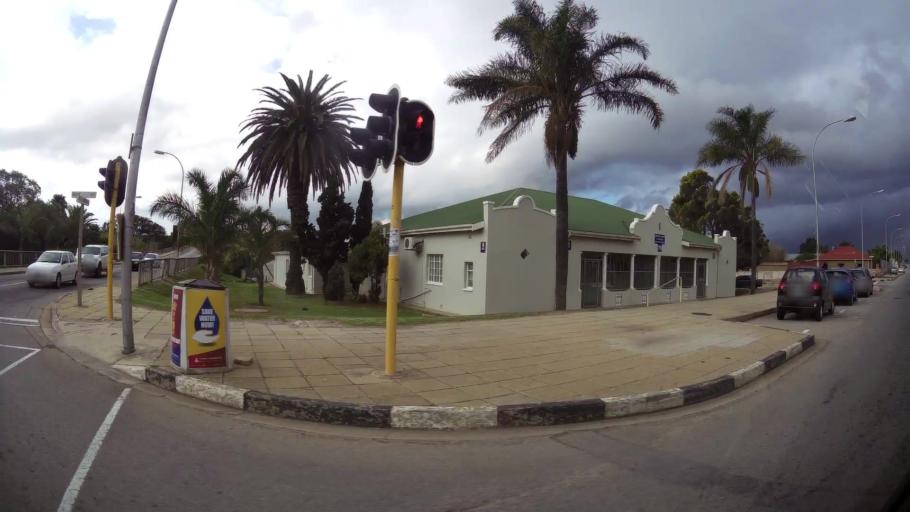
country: ZA
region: Eastern Cape
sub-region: Nelson Mandela Bay Metropolitan Municipality
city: Uitenhage
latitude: -33.8014
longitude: 25.4742
